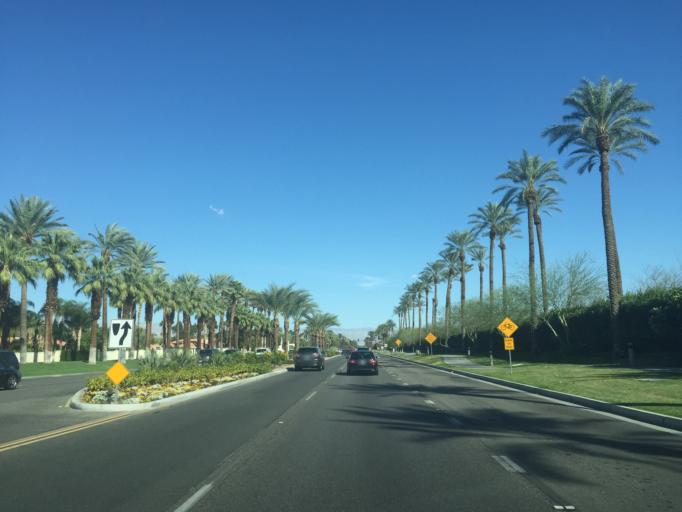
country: US
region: California
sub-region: Riverside County
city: Indian Wells
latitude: 33.7213
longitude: -116.3556
